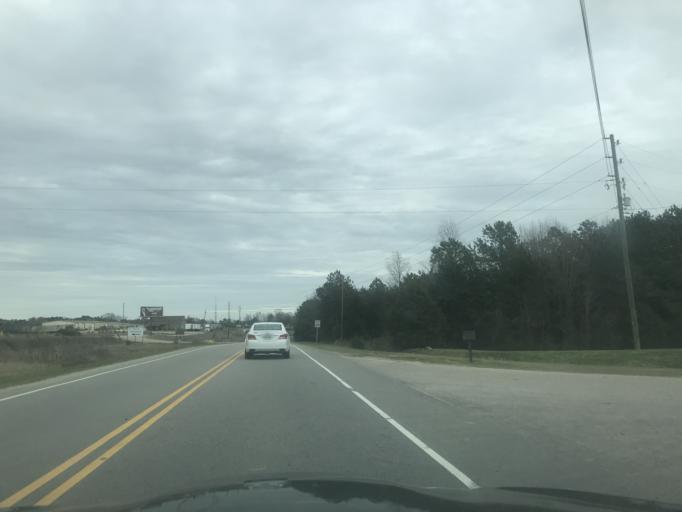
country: US
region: North Carolina
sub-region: Franklin County
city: Louisburg
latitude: 36.0835
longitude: -78.3358
